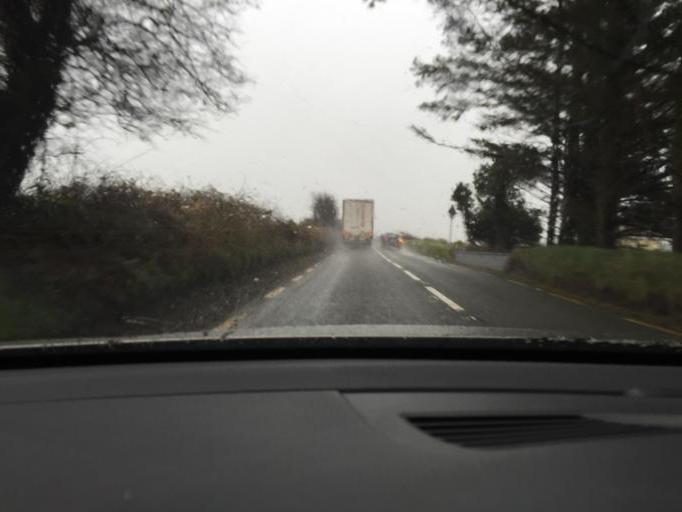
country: IE
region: Munster
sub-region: Ciarrai
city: Dingle
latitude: 52.1429
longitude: -10.1140
